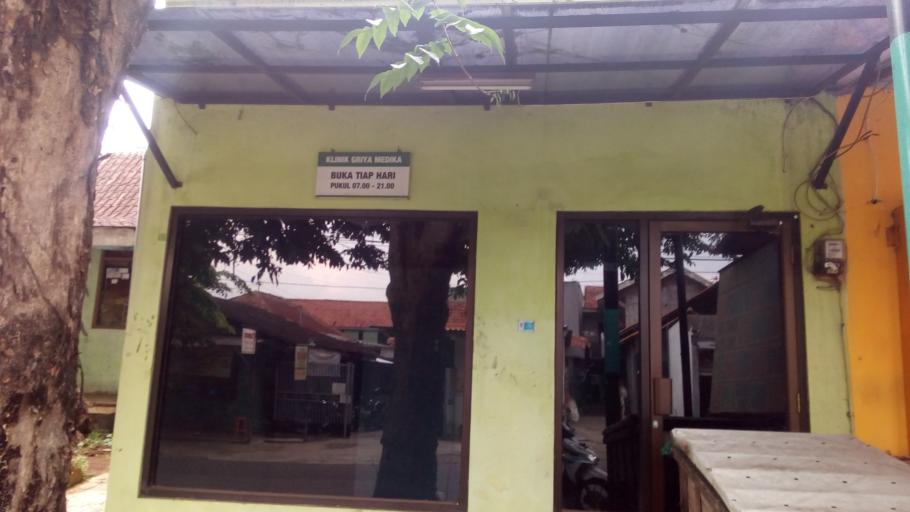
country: ID
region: Central Java
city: Semarang
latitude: -7.0599
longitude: 110.4399
